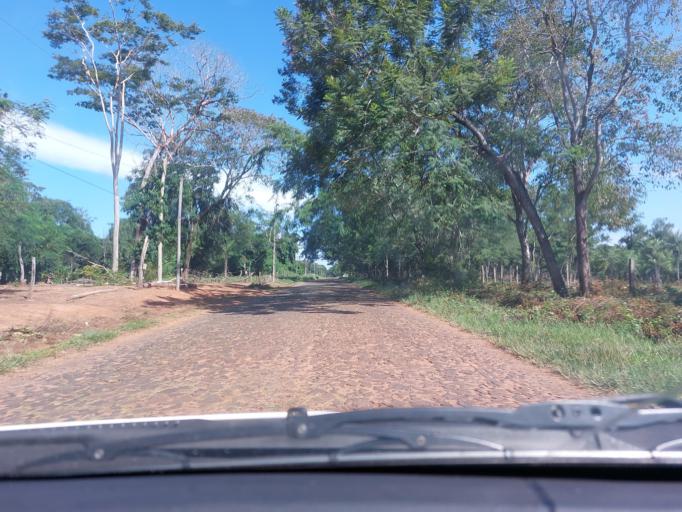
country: PY
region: San Pedro
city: Itacurubi del Rosario
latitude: -24.5718
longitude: -56.5971
